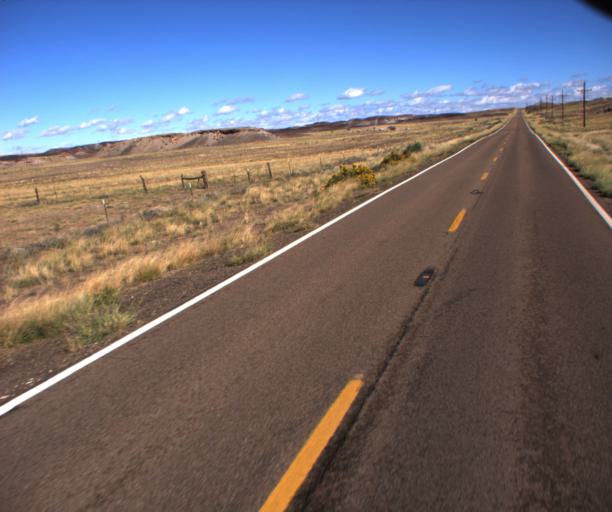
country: US
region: Arizona
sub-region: Apache County
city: Saint Johns
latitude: 34.5459
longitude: -109.3439
